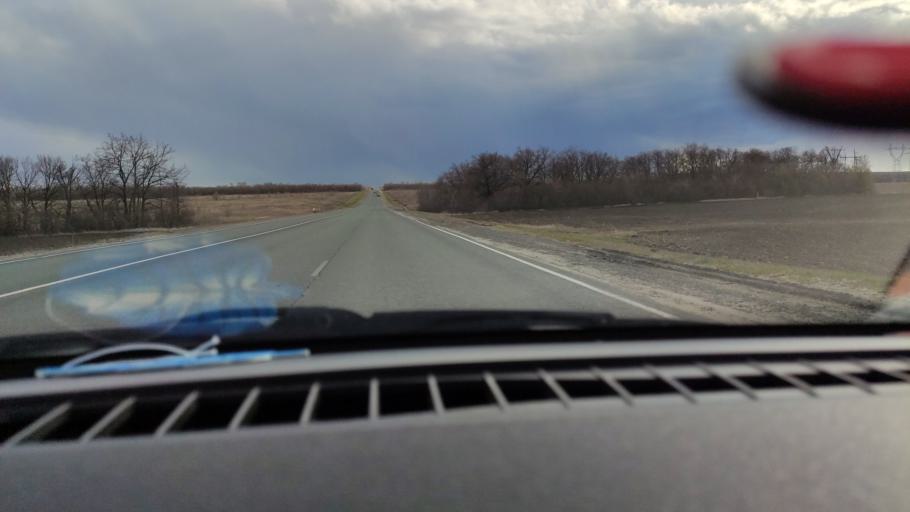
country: RU
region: Saratov
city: Sinodskoye
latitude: 51.9154
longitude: 46.5562
